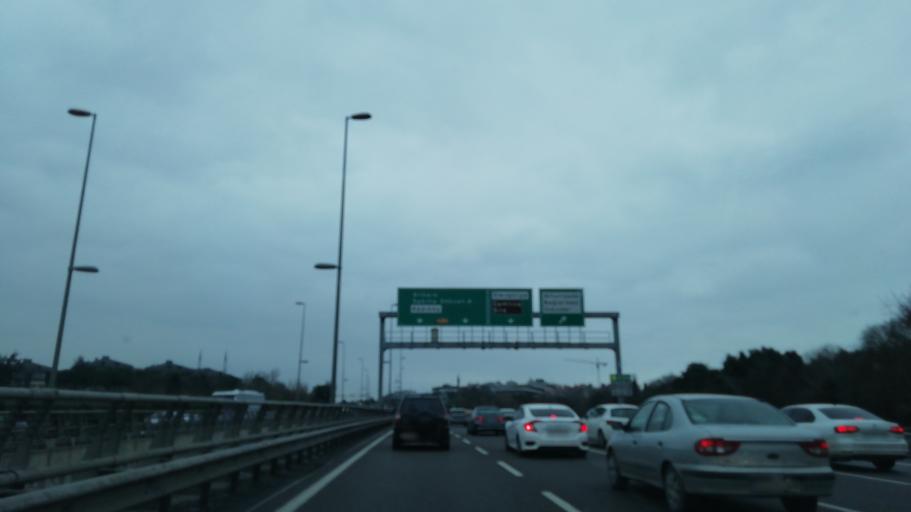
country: TR
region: Istanbul
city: UEskuedar
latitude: 41.0298
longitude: 29.0456
